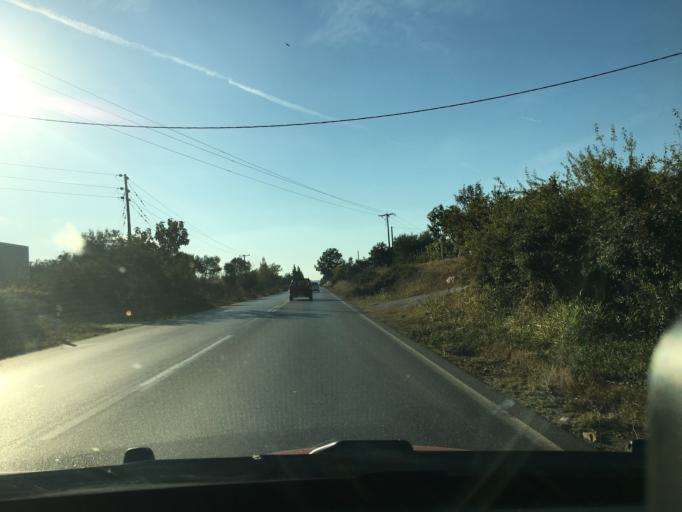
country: GR
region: Central Macedonia
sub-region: Nomos Chalkidikis
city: Kalyves Polygyrou
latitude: 40.2824
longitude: 23.4132
